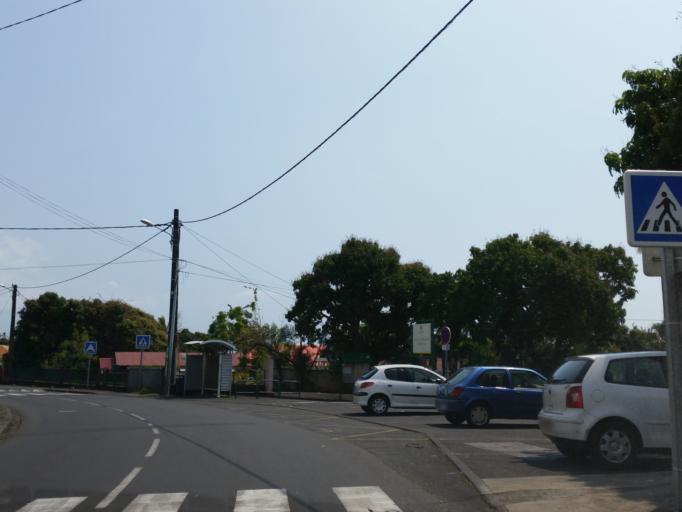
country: RE
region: Reunion
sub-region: Reunion
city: Sainte-Marie
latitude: -20.9124
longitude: 55.5067
